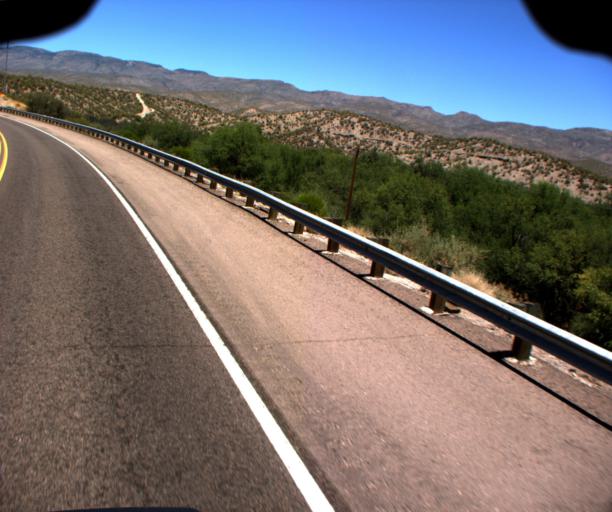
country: US
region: Arizona
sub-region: Pinal County
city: Kearny
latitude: 33.0881
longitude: -110.7152
